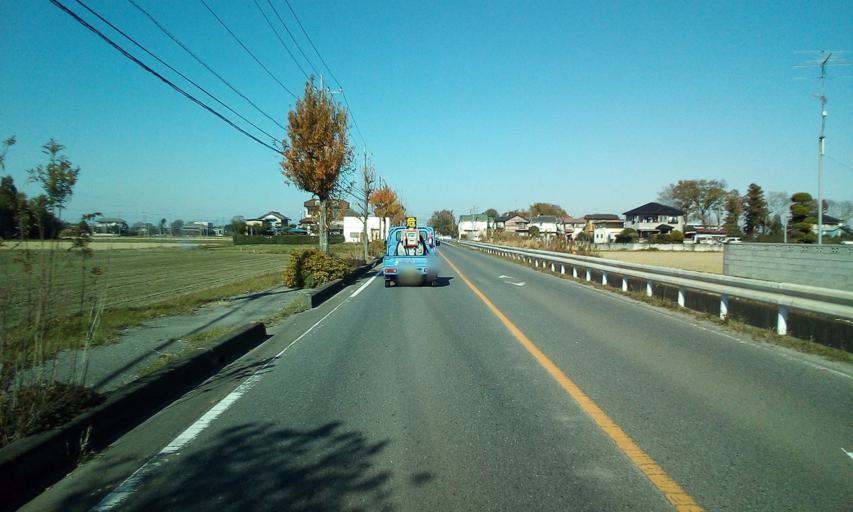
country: JP
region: Saitama
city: Kasukabe
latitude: 36.0202
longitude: 139.7905
